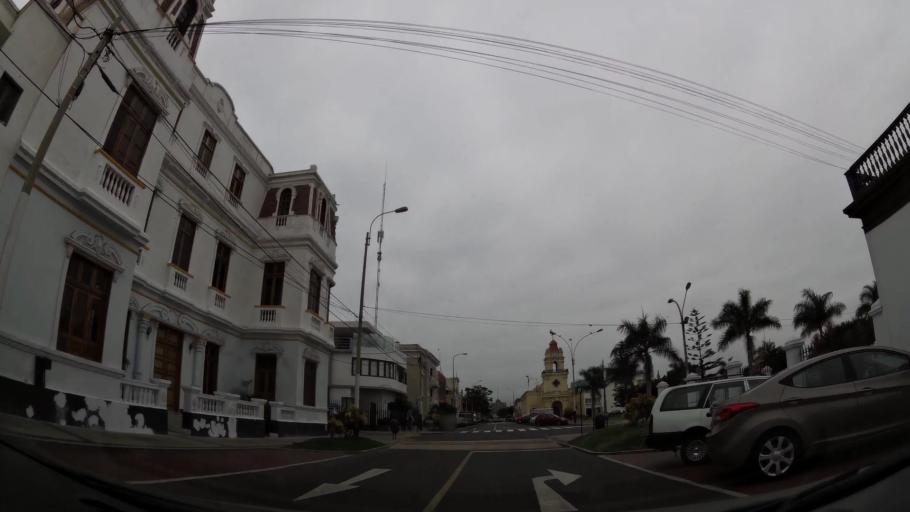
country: PE
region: Callao
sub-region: Callao
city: Callao
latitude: -12.0727
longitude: -77.1650
